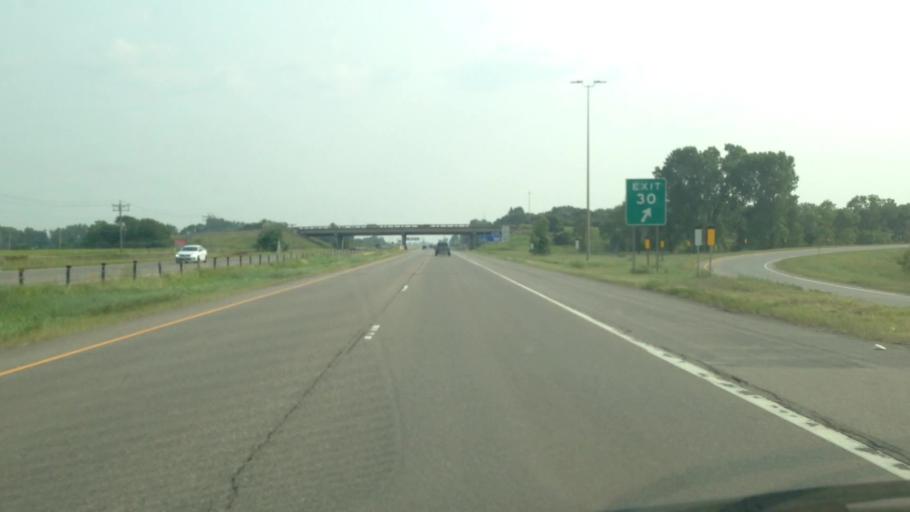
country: US
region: Minnesota
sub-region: Ramsey County
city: Mounds View
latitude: 45.1187
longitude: -93.1887
